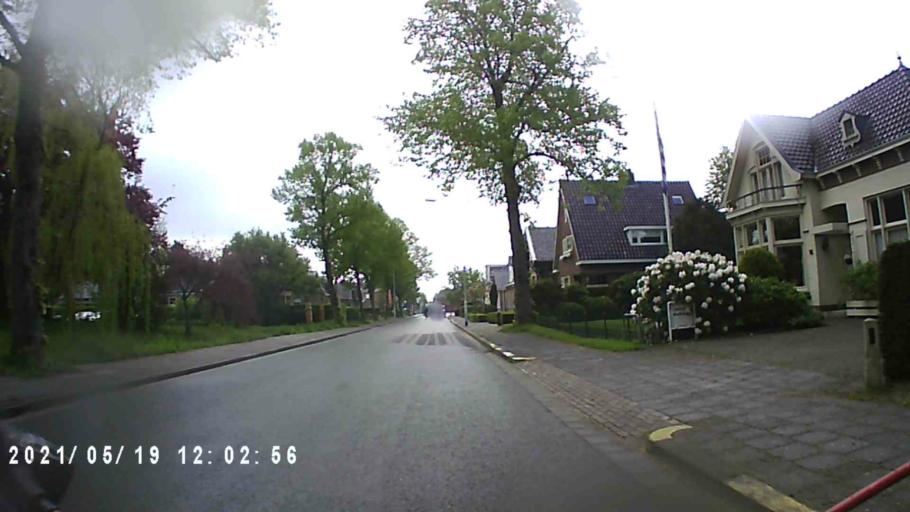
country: NL
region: Friesland
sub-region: Gemeente Achtkarspelen
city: Buitenpost
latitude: 53.2554
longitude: 6.1426
